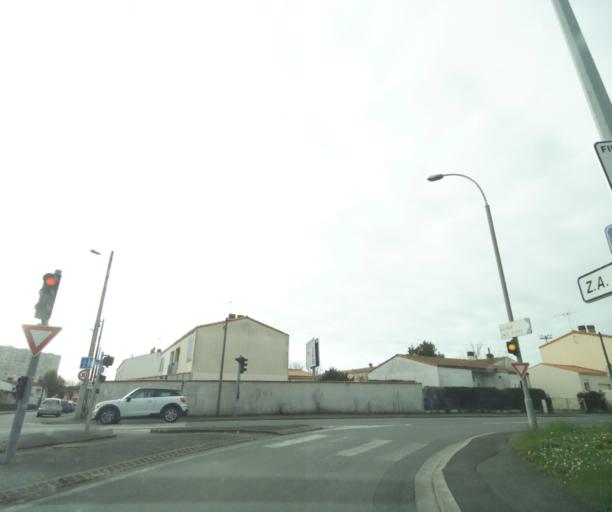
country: FR
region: Poitou-Charentes
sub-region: Departement de la Charente-Maritime
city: La Rochelle
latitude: 46.1718
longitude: -1.1737
